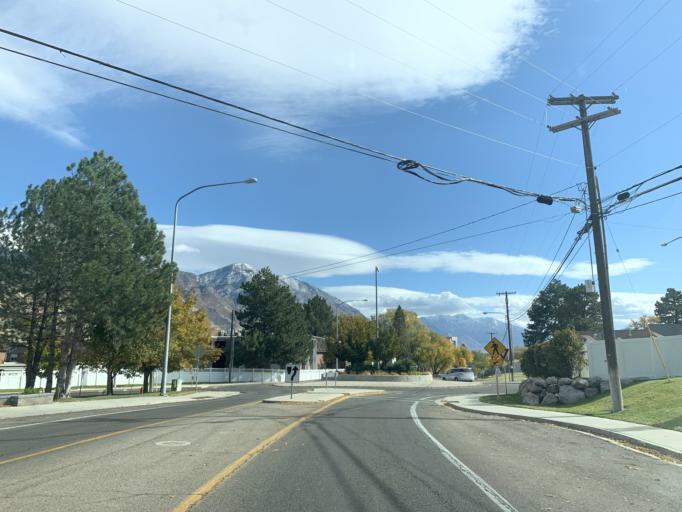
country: US
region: Utah
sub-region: Utah County
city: Provo
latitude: 40.2572
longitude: -111.6759
